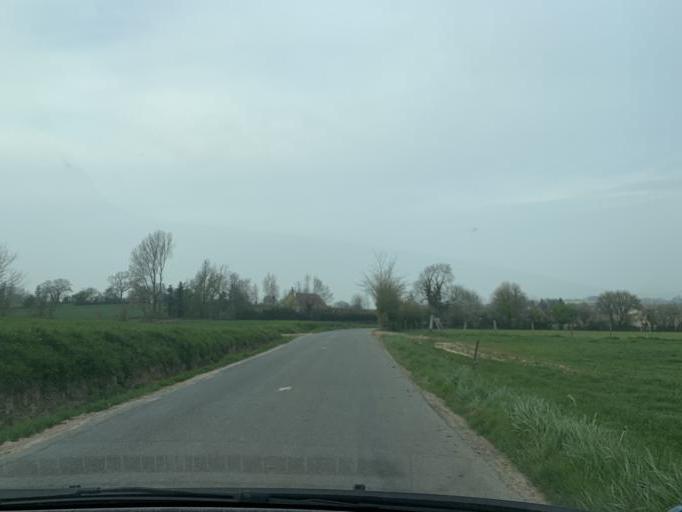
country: FR
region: Nord-Pas-de-Calais
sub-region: Departement du Pas-de-Calais
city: Samer
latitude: 50.6766
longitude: 1.7557
